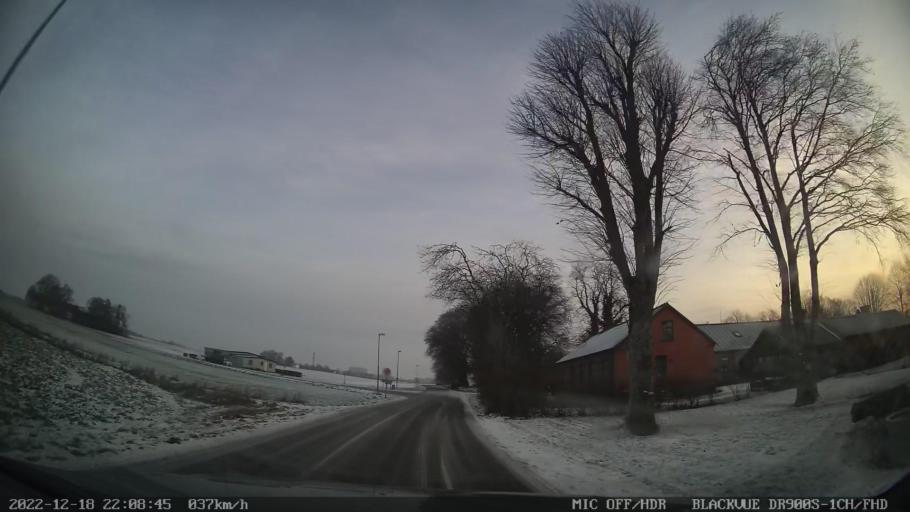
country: SE
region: Skane
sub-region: Tomelilla Kommun
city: Tomelilla
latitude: 55.5281
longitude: 14.0410
